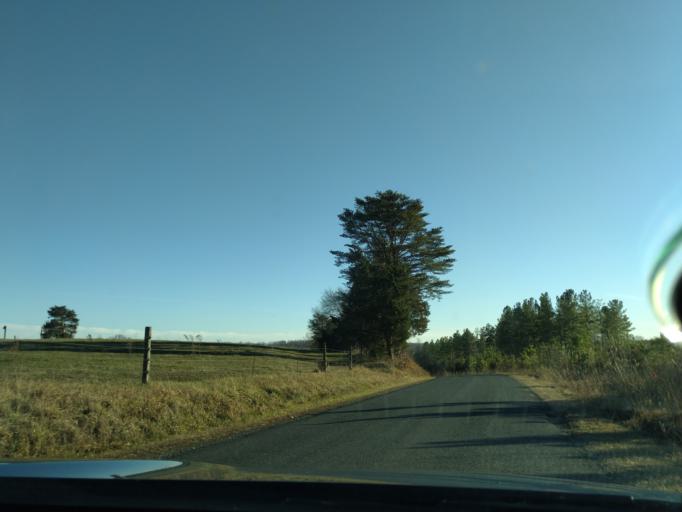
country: US
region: Virginia
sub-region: Prince Edward County
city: Hampden Sydney
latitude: 37.3577
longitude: -78.6030
